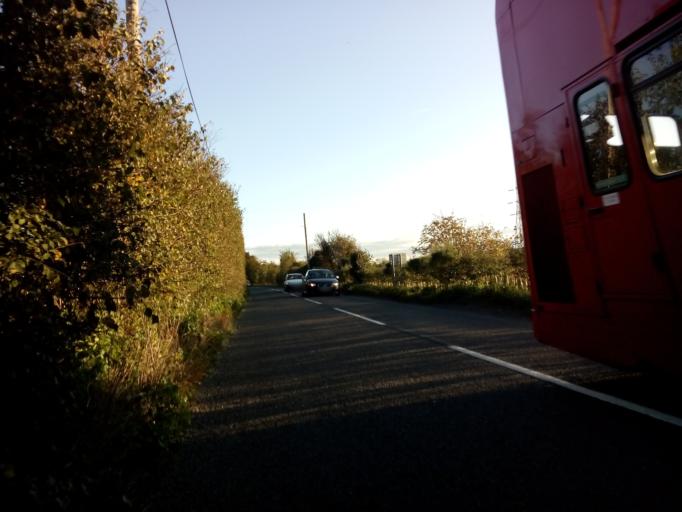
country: GB
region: England
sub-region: Suffolk
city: Sudbury
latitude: 51.9983
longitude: 0.7621
